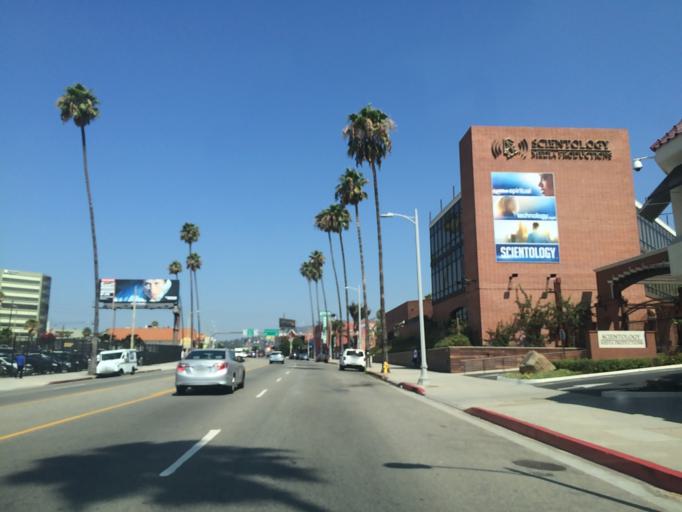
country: US
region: California
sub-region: Los Angeles County
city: Silver Lake
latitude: 34.0967
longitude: -118.2851
